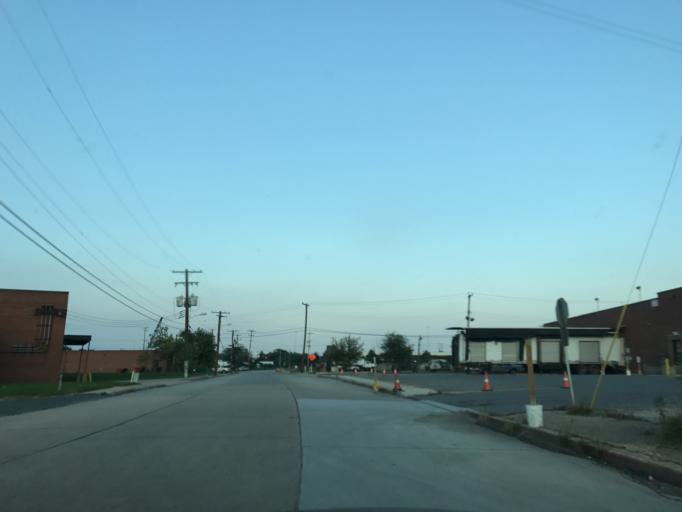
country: US
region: Maryland
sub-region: Baltimore County
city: Rosedale
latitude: 39.2995
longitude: -76.5383
